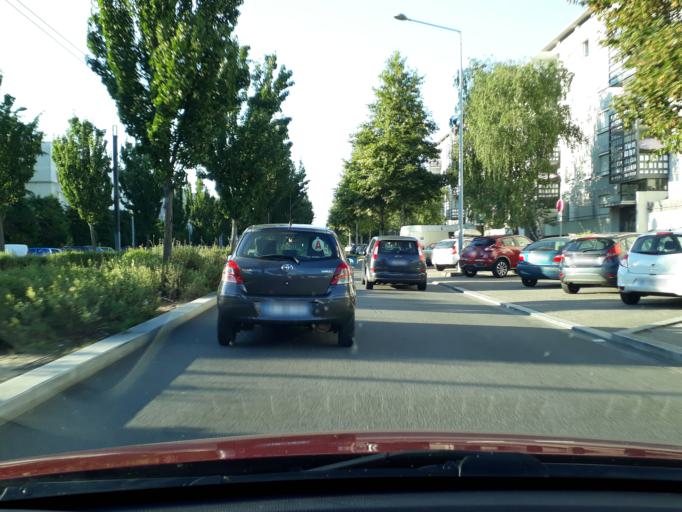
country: FR
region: Rhone-Alpes
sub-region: Departement du Rhone
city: Venissieux
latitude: 45.6976
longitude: 4.8878
